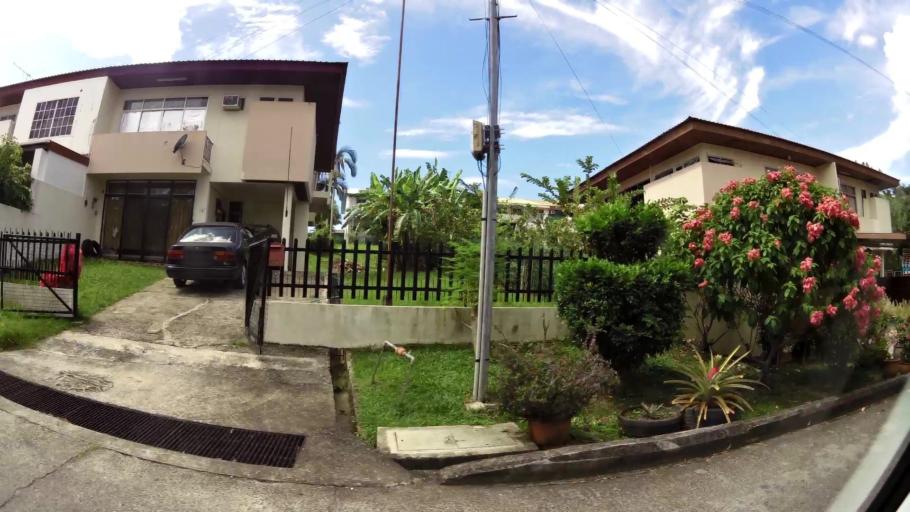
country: BN
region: Brunei and Muara
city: Bandar Seri Begawan
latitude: 4.9669
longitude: 114.9494
